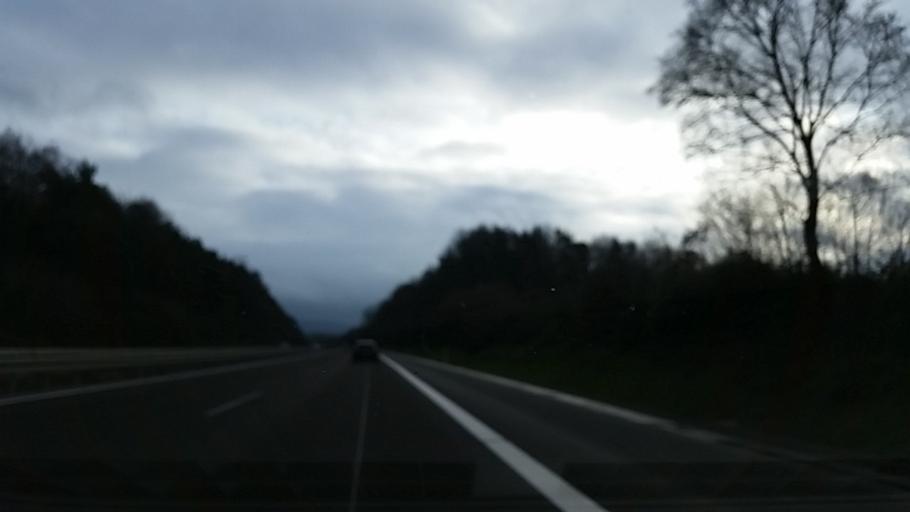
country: DE
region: Hesse
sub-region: Regierungsbezirk Kassel
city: Eichenzell
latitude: 50.4603
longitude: 9.7226
